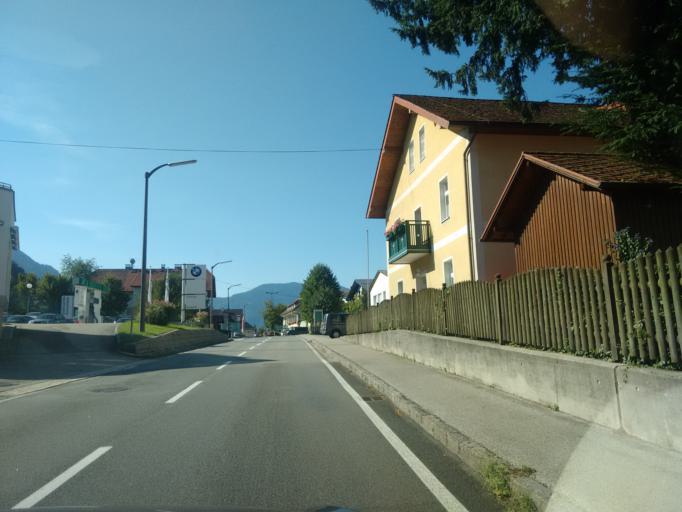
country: AT
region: Upper Austria
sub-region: Politischer Bezirk Vocklabruck
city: Steinbach am Attersee
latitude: 47.8413
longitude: 13.5470
